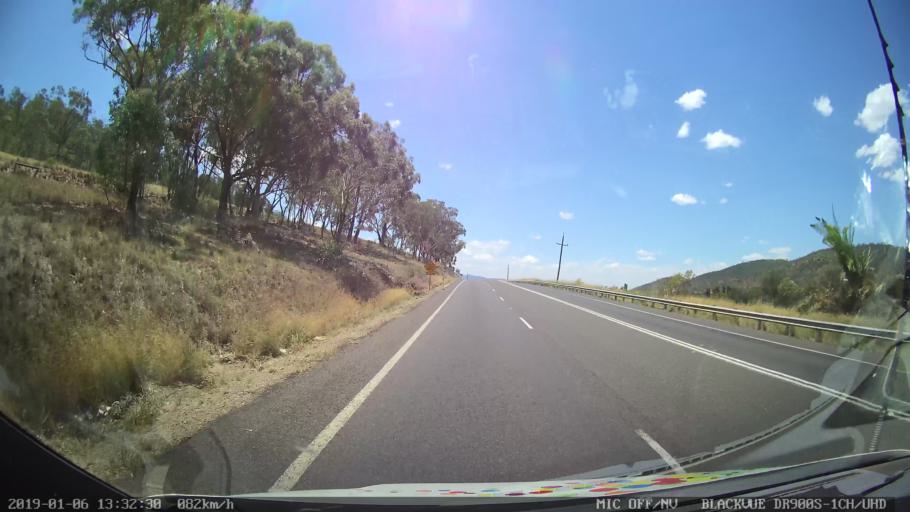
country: AU
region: New South Wales
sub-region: Tamworth Municipality
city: East Tamworth
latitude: -31.1095
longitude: 150.9988
